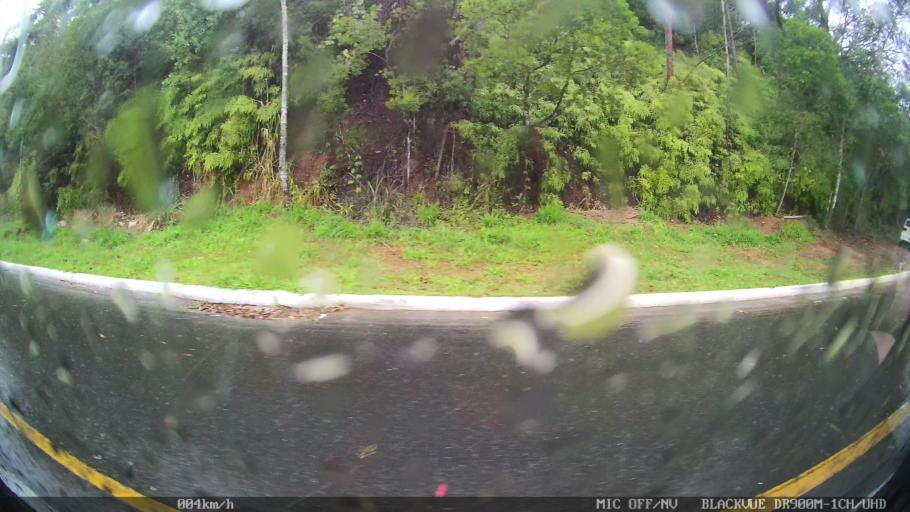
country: BR
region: Santa Catarina
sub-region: Itajai
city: Itajai
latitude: -26.9351
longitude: -48.6403
